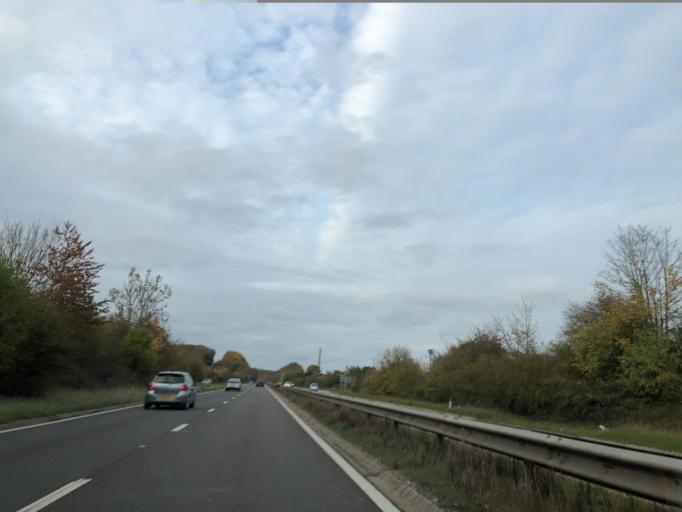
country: GB
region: England
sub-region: Buckinghamshire
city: Marlow
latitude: 51.5817
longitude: -0.7570
